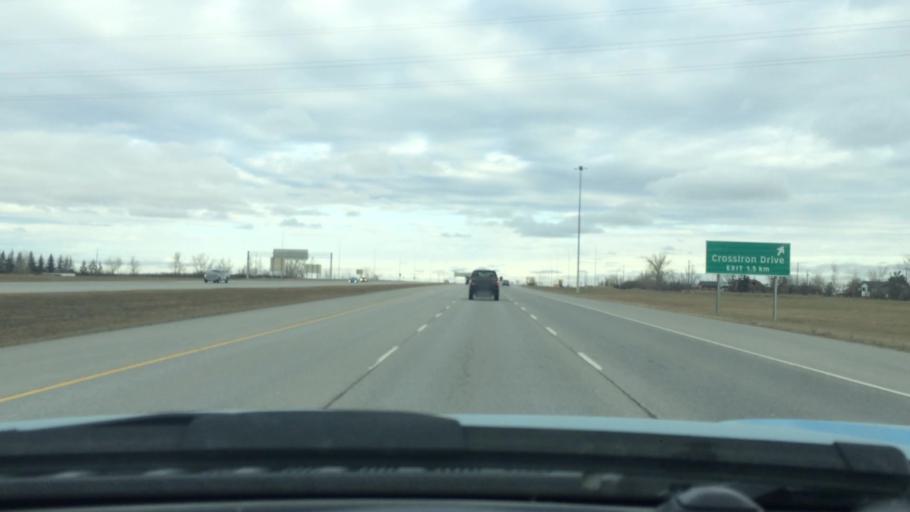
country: CA
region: Alberta
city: Airdrie
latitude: 51.1794
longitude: -114.0007
